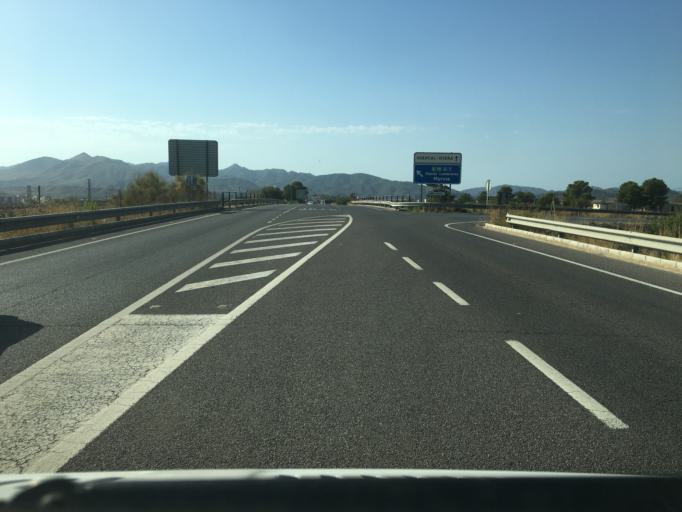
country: ES
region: Andalusia
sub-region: Provincia de Almeria
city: Huercal-Overa
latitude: 37.4081
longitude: -1.9590
